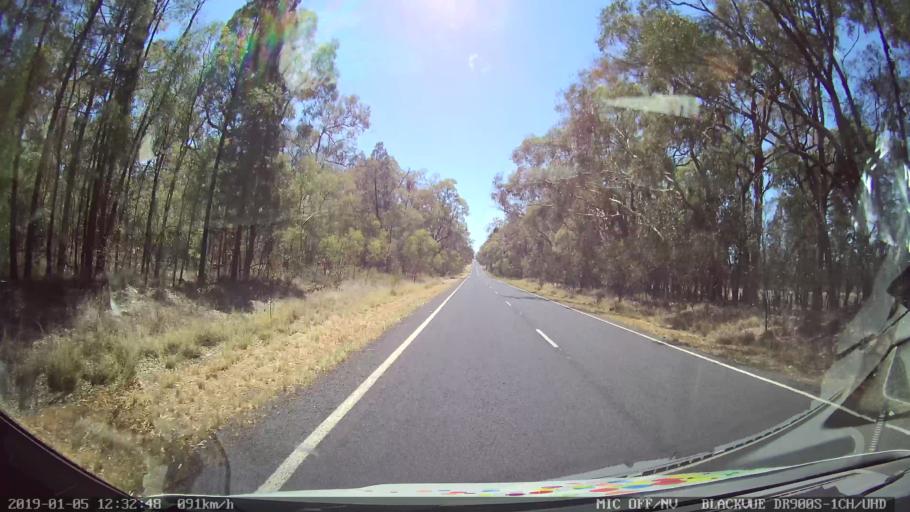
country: AU
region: New South Wales
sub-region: Warrumbungle Shire
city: Coonabarabran
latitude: -31.2165
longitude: 149.3851
